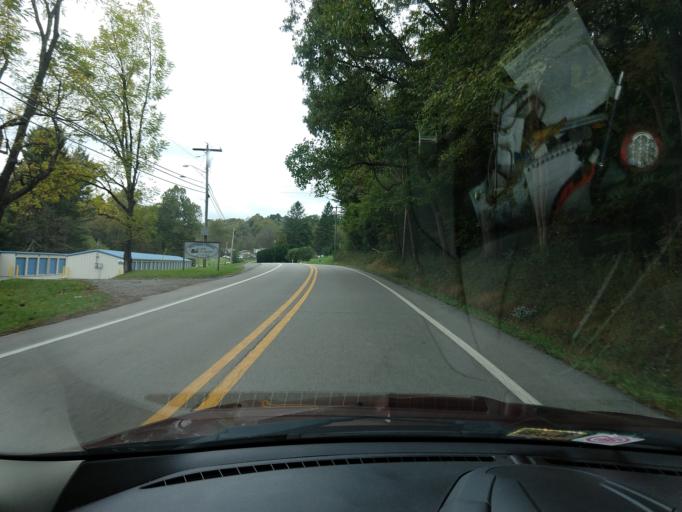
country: US
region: West Virginia
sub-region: Barbour County
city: Belington
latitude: 38.9989
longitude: -79.9355
